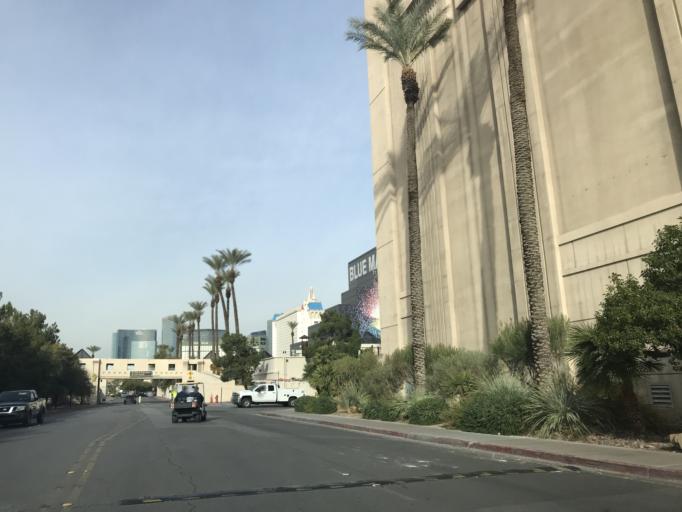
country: US
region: Nevada
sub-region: Clark County
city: Paradise
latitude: 36.0945
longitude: -115.1780
